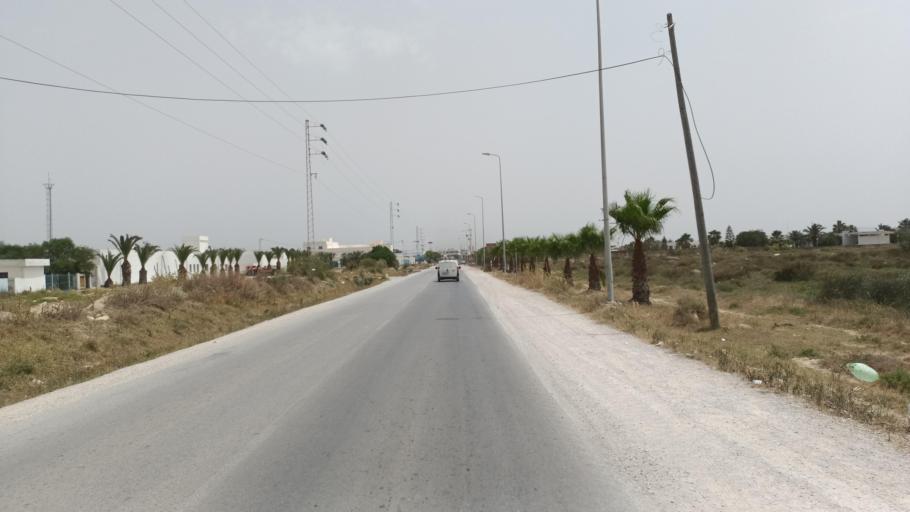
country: TN
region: Nabul
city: Manzil Bu Zalafah
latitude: 36.7121
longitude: 10.4813
